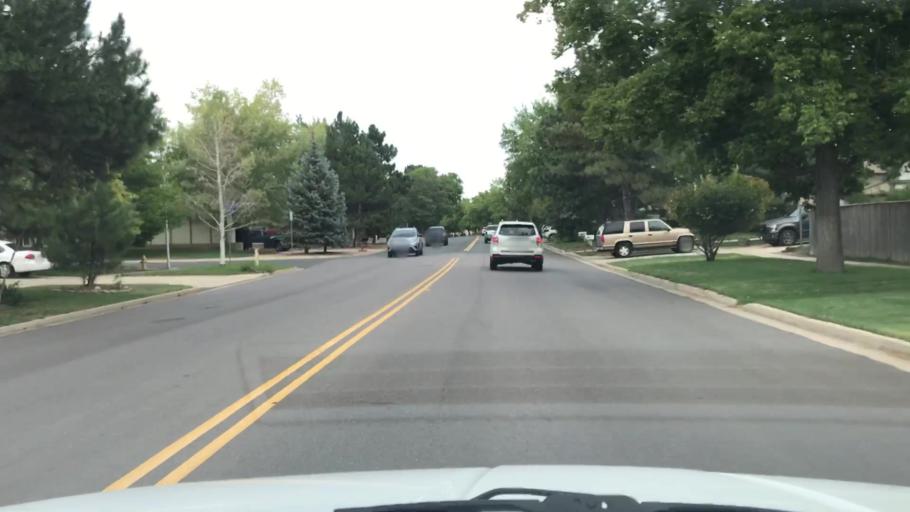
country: US
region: Colorado
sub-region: Broomfield County
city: Broomfield
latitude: 39.9331
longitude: -105.0815
